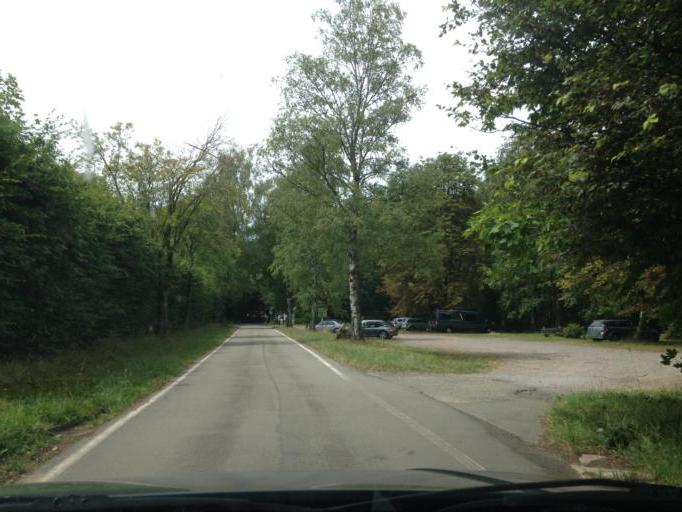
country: DE
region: Rheinland-Pfalz
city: Eusserthal
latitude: 49.2844
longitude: 7.9145
